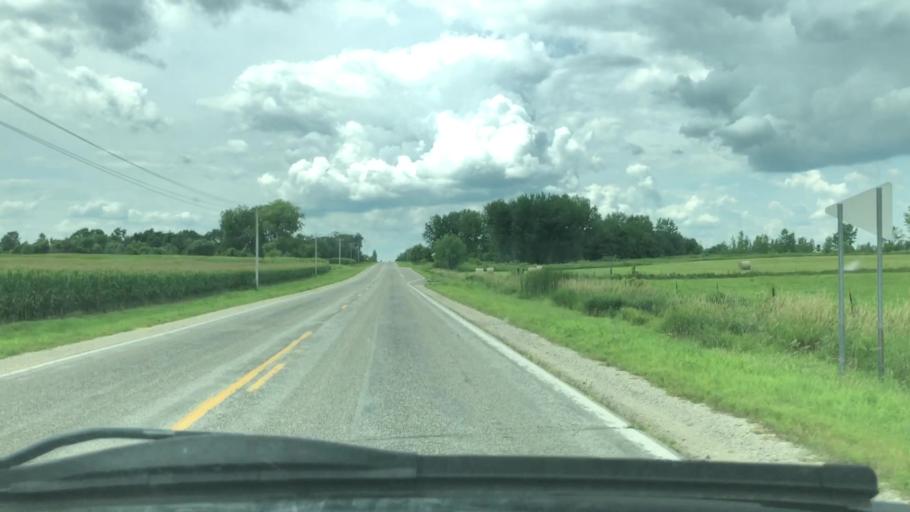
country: US
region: Minnesota
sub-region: Olmsted County
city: Stewartville
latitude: 43.8627
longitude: -92.5139
